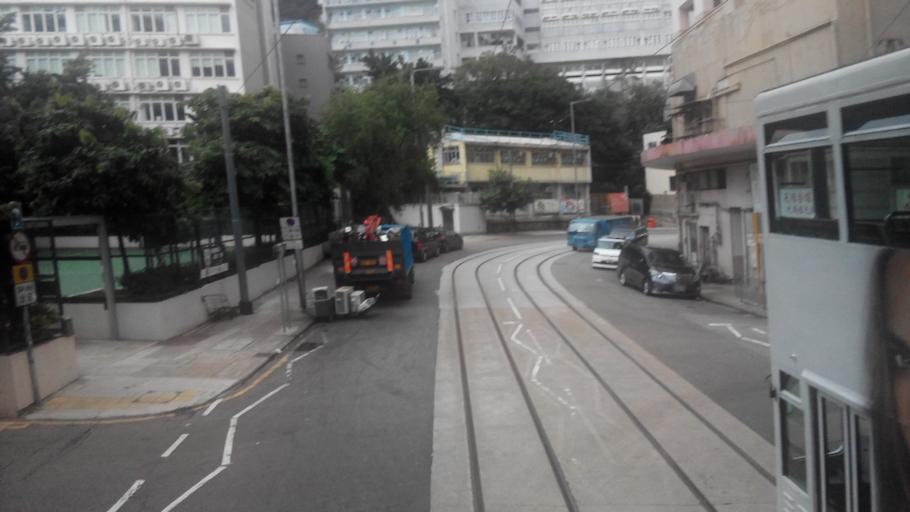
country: HK
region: Wanchai
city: Wan Chai
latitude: 22.2773
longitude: 114.2300
